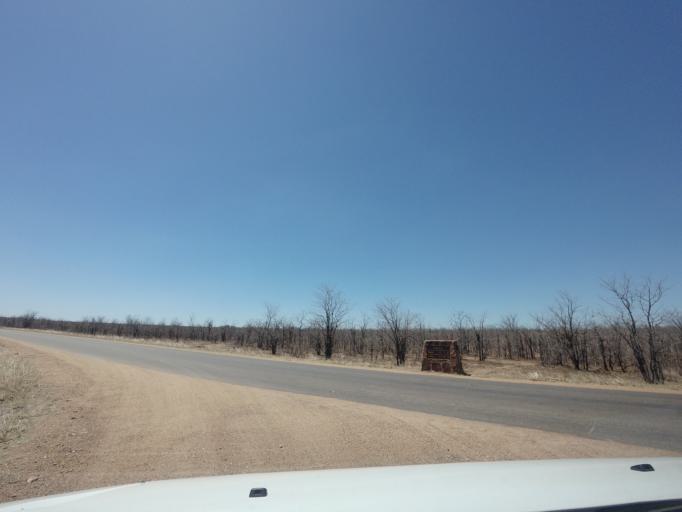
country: ZA
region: Limpopo
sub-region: Mopani District Municipality
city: Phalaborwa
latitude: -23.5395
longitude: 31.4238
